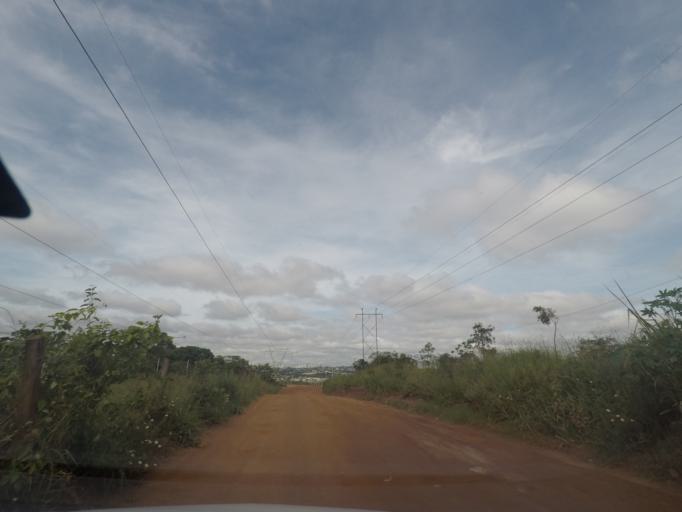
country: BR
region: Goias
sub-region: Goiania
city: Goiania
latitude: -16.6731
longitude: -49.1861
